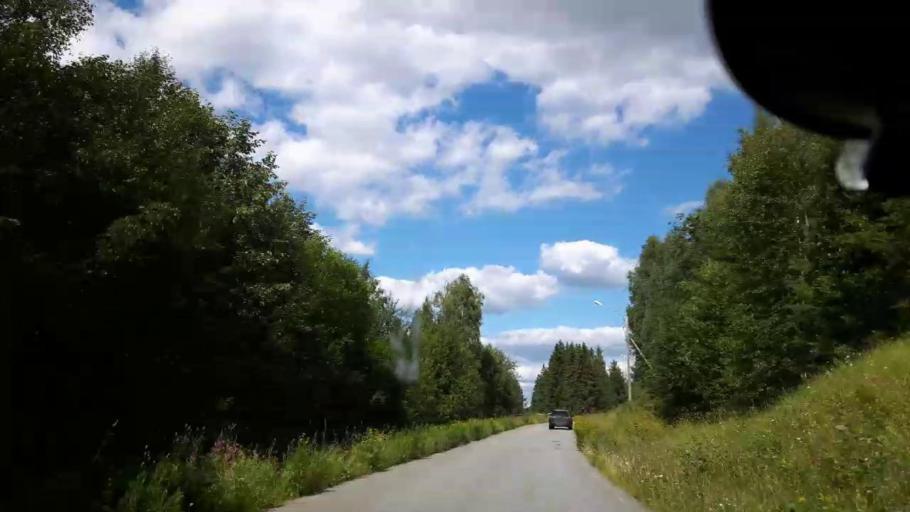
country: SE
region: Jaemtland
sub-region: Ragunda Kommun
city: Hammarstrand
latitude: 62.9444
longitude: 16.6904
